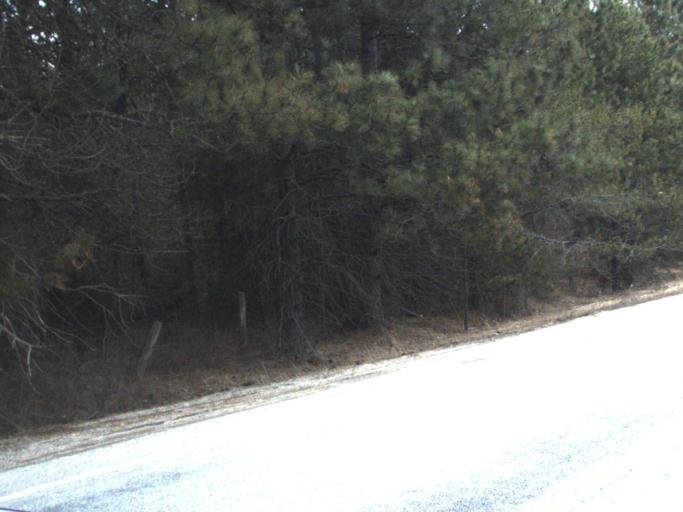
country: US
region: Washington
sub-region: Pend Oreille County
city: Newport
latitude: 48.2313
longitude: -117.1672
